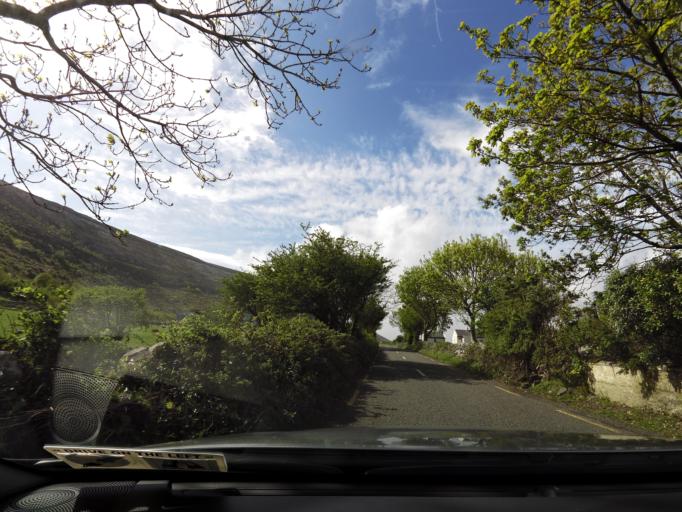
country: IE
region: Connaught
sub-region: County Galway
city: Bearna
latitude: 53.1397
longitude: -9.2242
